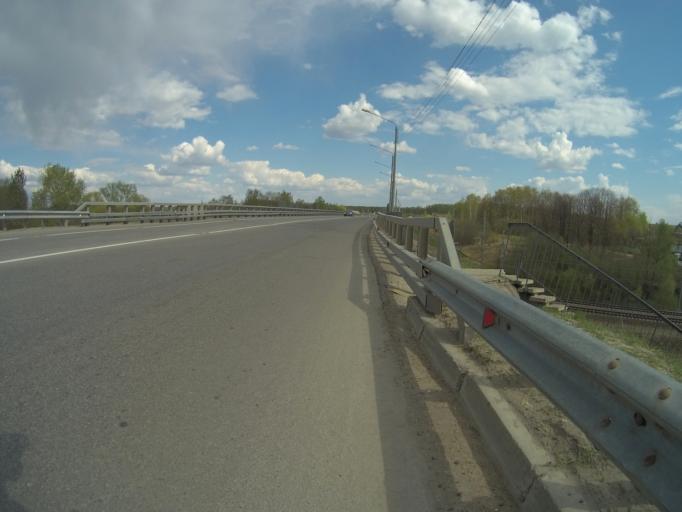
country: RU
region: Vladimir
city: Orgtrud
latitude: 56.2110
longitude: 40.5860
